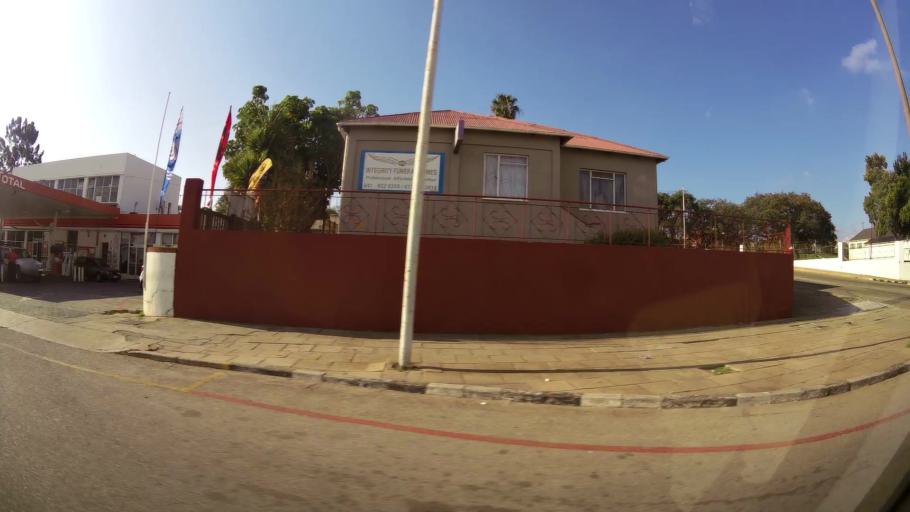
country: ZA
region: Eastern Cape
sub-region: Nelson Mandela Bay Metropolitan Municipality
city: Uitenhage
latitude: -33.7690
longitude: 25.4036
